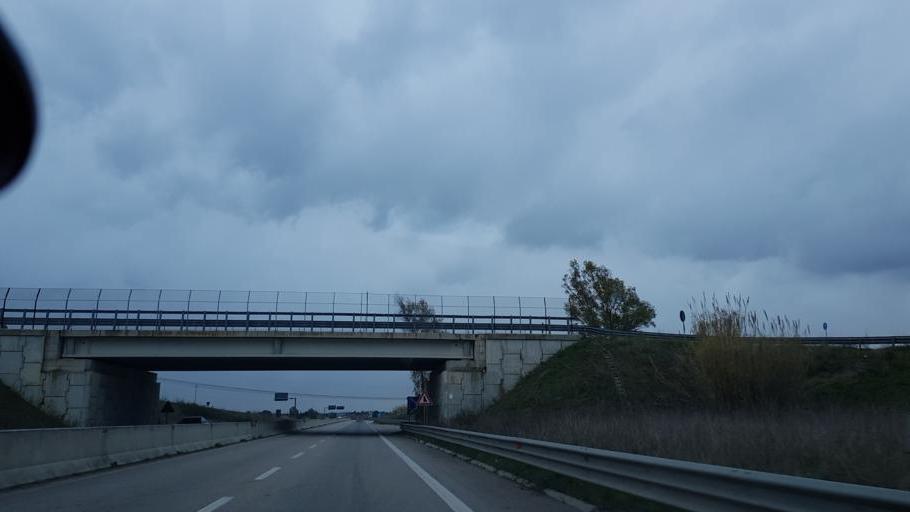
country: IT
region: Apulia
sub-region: Provincia di Brindisi
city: Brindisi
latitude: 40.6048
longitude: 17.8833
